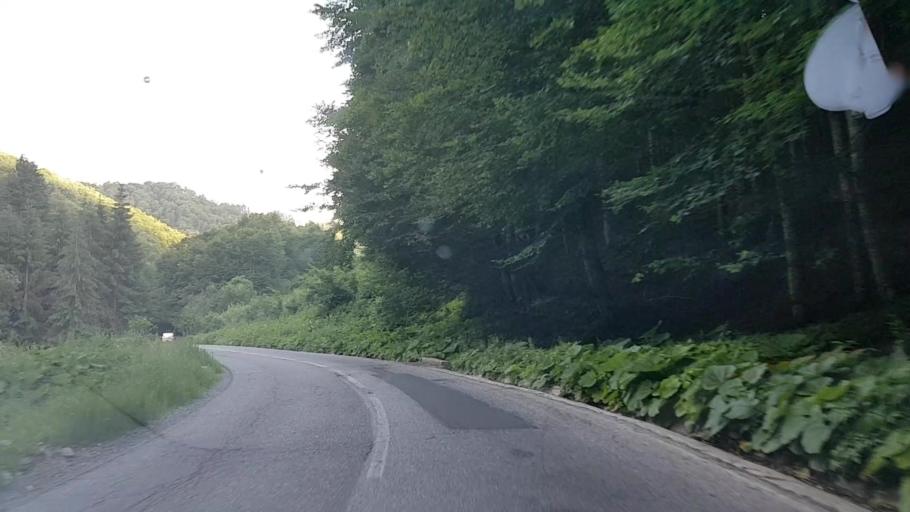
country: RO
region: Harghita
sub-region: Comuna Praid
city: Ocna de Sus
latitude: 46.5948
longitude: 25.2416
